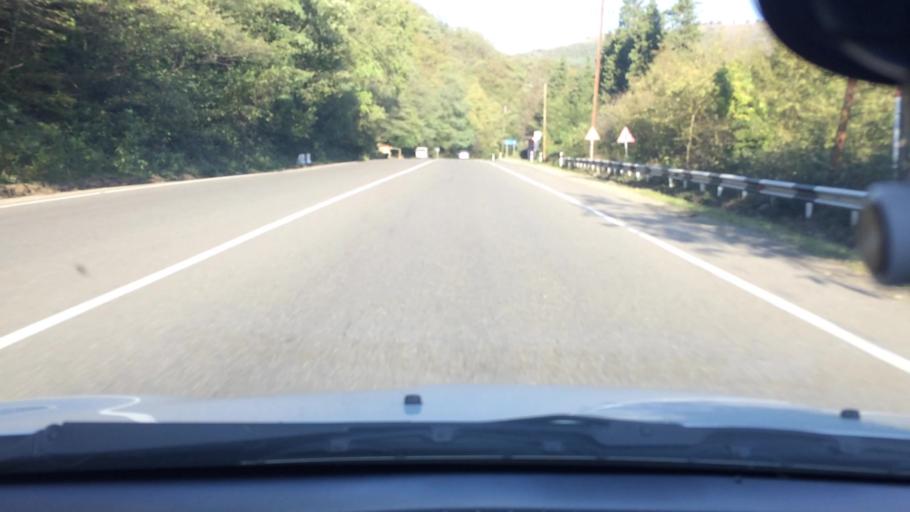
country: GE
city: Shorapani
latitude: 42.0911
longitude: 43.1321
